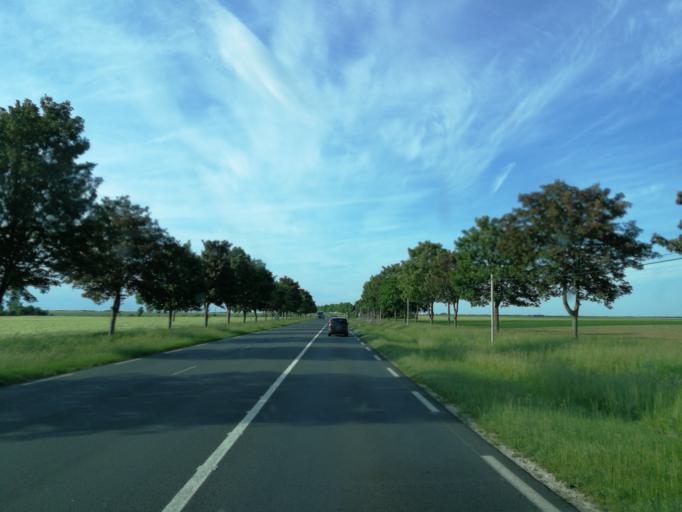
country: FR
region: Centre
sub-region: Departement d'Eure-et-Loir
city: Bonneval
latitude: 48.2129
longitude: 1.4008
